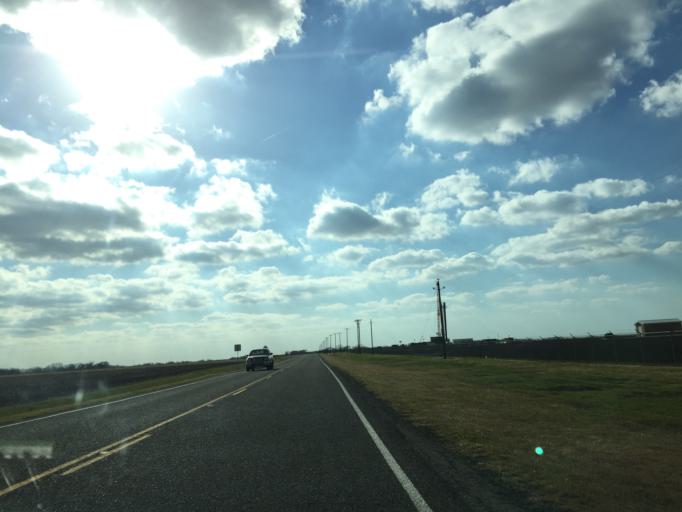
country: US
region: Texas
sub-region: Williamson County
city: Granger
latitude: 30.6545
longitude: -97.3813
